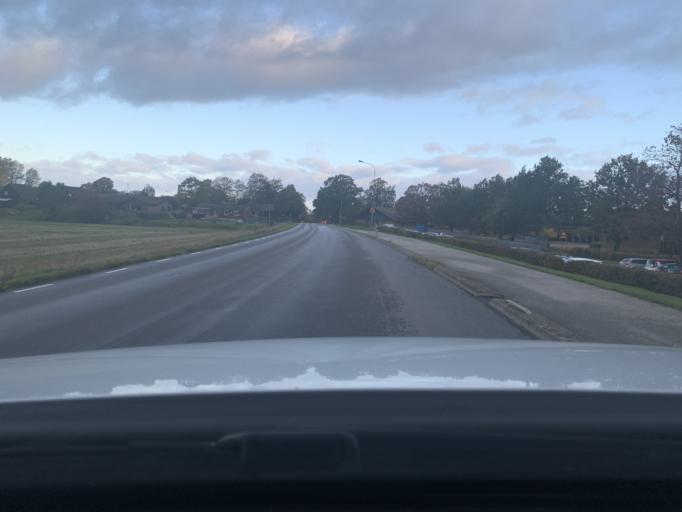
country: SE
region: Skane
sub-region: Horby Kommun
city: Hoerby
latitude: 55.8400
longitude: 13.6582
